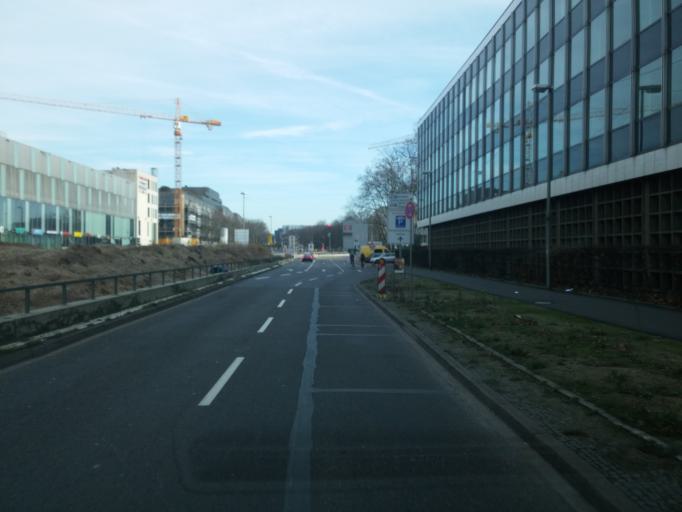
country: DE
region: Baden-Wuerttemberg
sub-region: Karlsruhe Region
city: Karlsruhe
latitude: 49.0053
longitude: 8.4012
